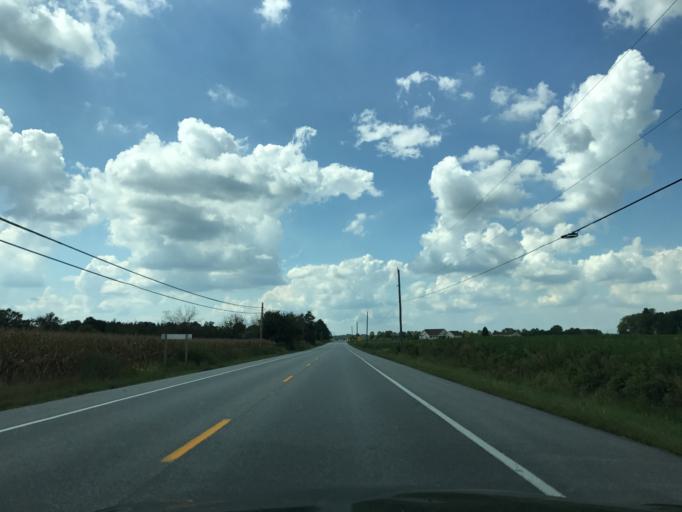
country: US
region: Maryland
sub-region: Queen Anne's County
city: Kingstown
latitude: 39.1861
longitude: -75.8665
